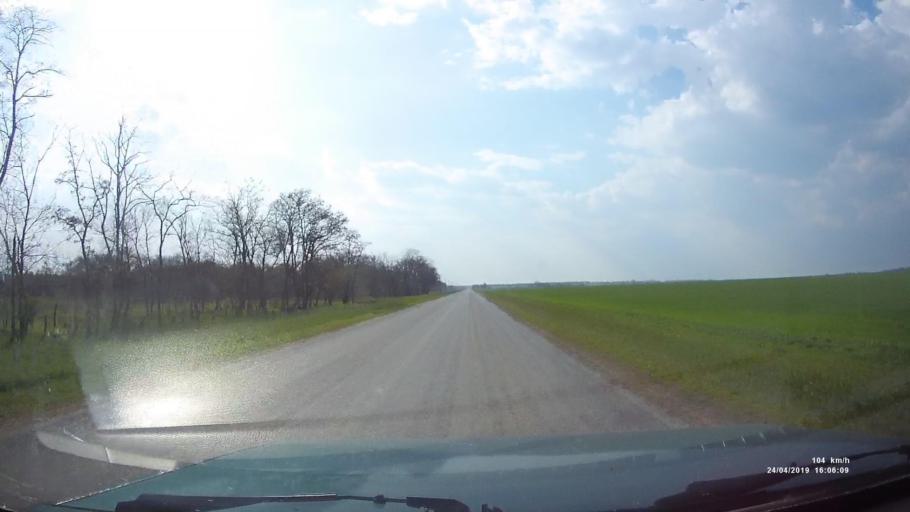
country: RU
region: Rostov
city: Sovetskoye
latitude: 46.6849
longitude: 42.3551
